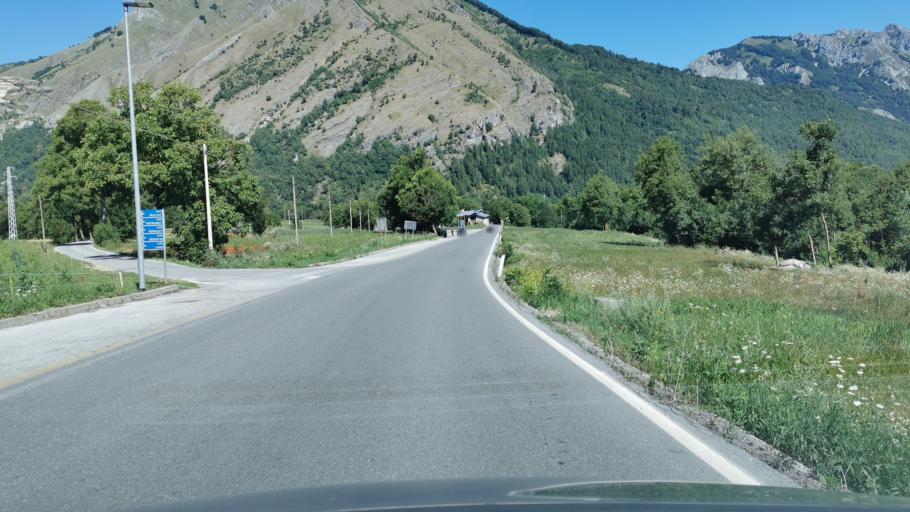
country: IT
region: Piedmont
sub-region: Provincia di Cuneo
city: Entracque
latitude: 44.2558
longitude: 7.3847
